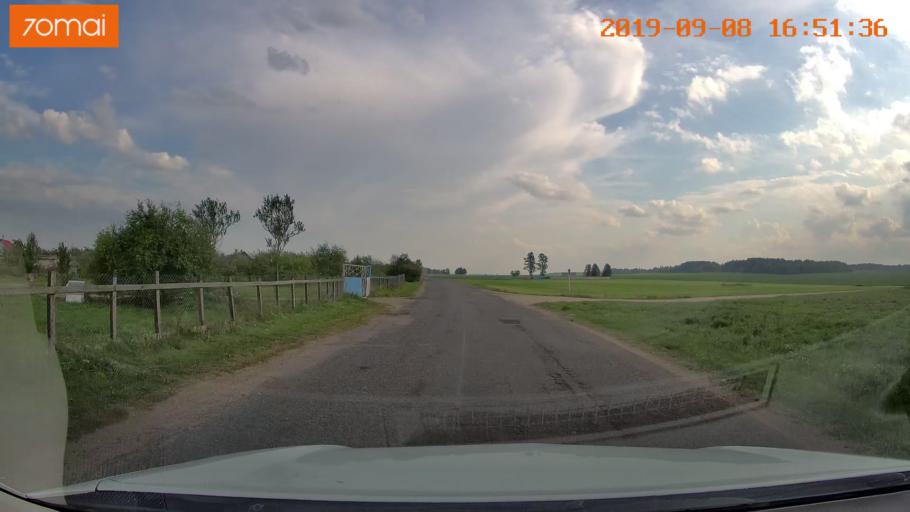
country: BY
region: Grodnenskaya
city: Hrodna
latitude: 53.7843
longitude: 23.8948
